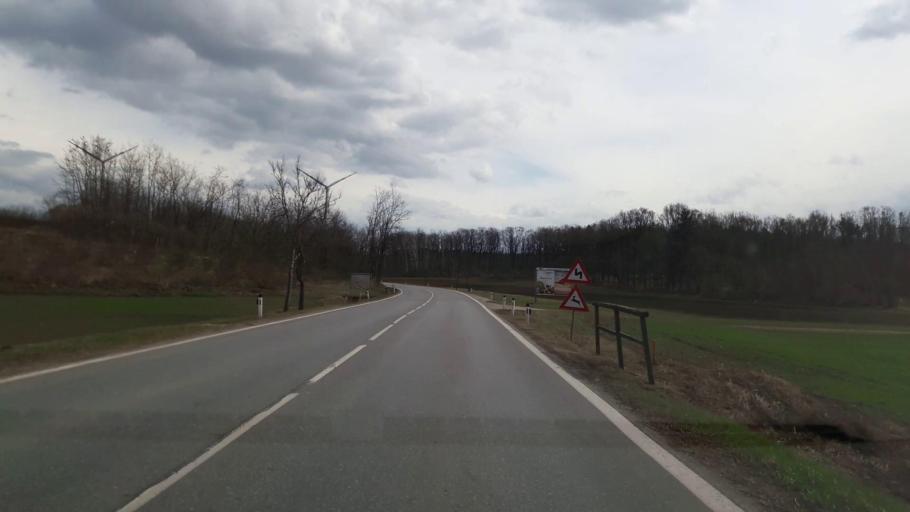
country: AT
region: Lower Austria
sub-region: Politischer Bezirk Mistelbach
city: Mistelbach
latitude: 48.5411
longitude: 16.5922
